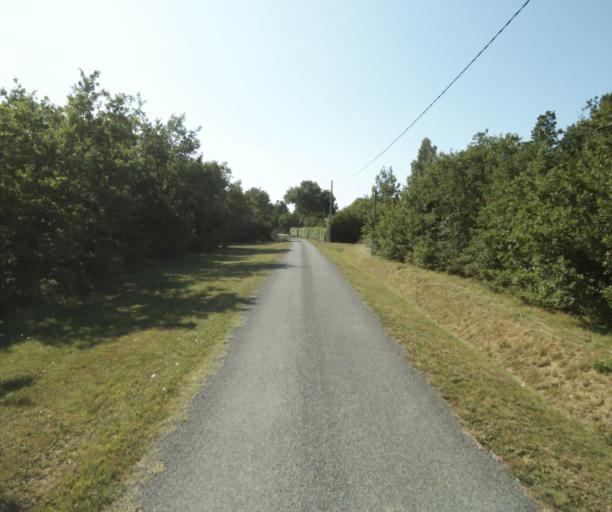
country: FR
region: Midi-Pyrenees
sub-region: Departement de la Haute-Garonne
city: Saint-Felix-Lauragais
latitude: 43.4276
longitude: 1.8382
